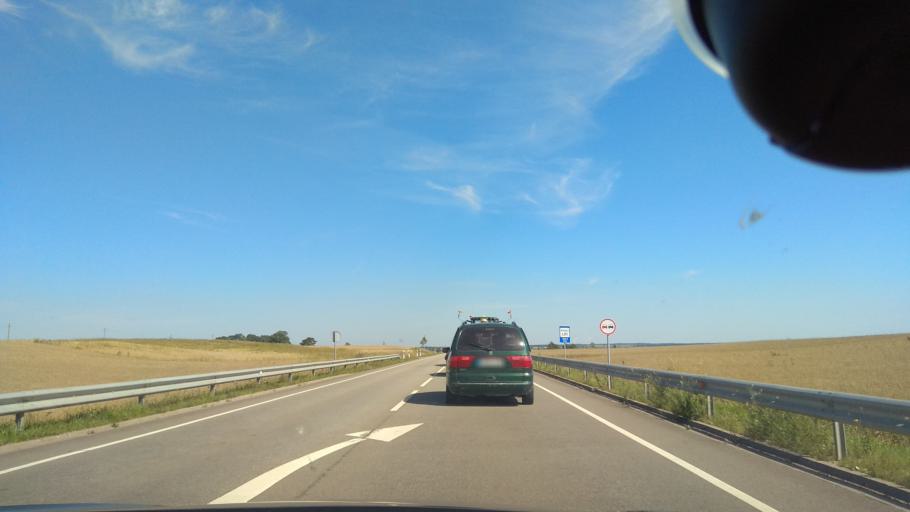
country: LT
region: Telsiu apskritis
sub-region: Telsiai
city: Telsiai
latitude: 56.0051
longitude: 22.2929
